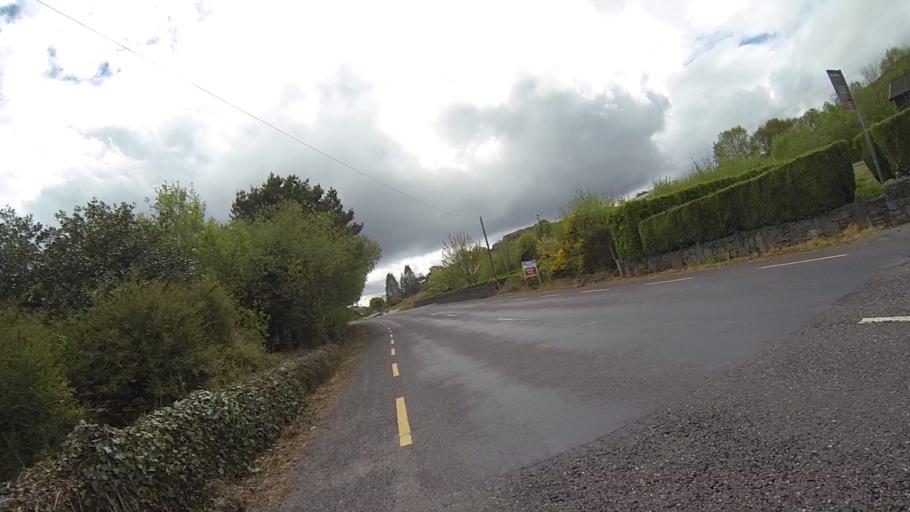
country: IE
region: Munster
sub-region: County Cork
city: Bantry
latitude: 51.7438
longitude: -9.5511
